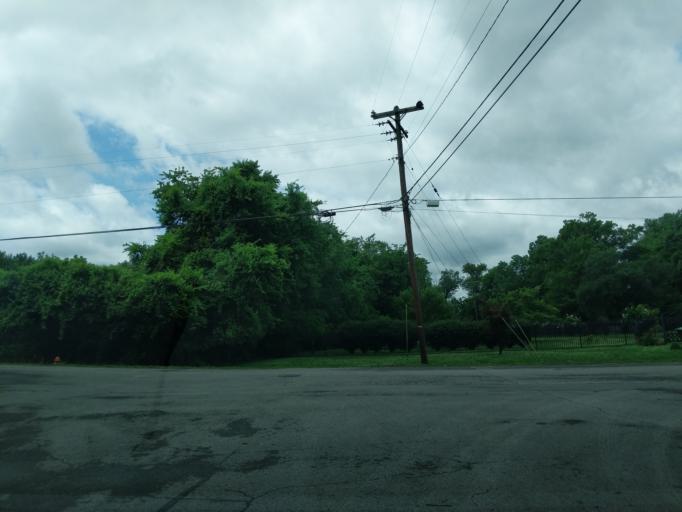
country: US
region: Tennessee
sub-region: Davidson County
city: Lakewood
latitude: 36.2405
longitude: -86.6802
